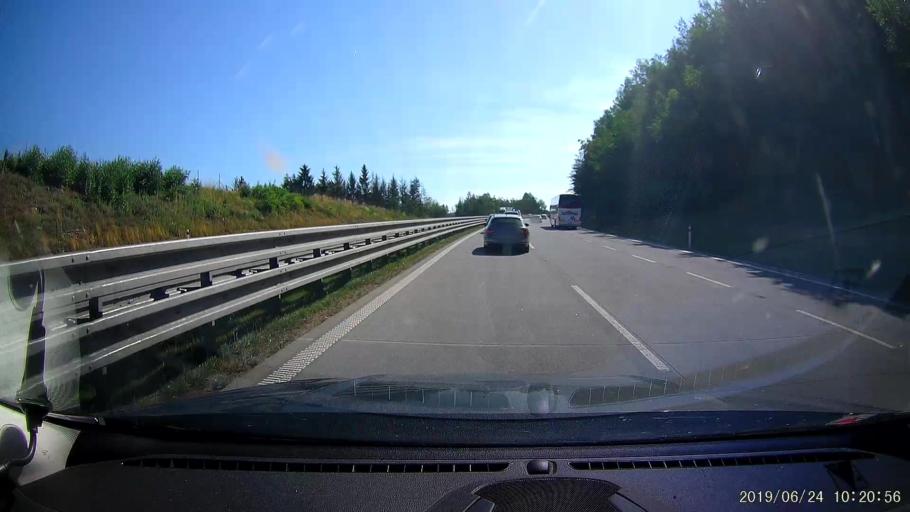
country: CZ
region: Vysocina
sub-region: Okres Pelhrimov
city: Zeliv
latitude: 49.5986
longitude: 15.2202
